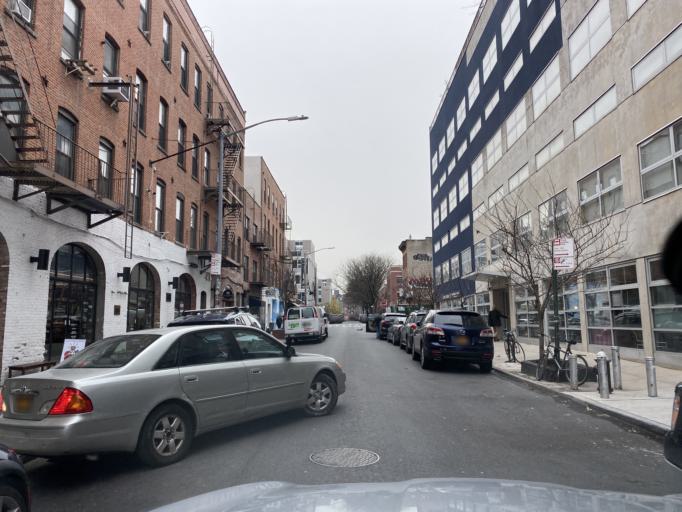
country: US
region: New York
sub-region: Queens County
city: Long Island City
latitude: 40.7169
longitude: -73.9622
